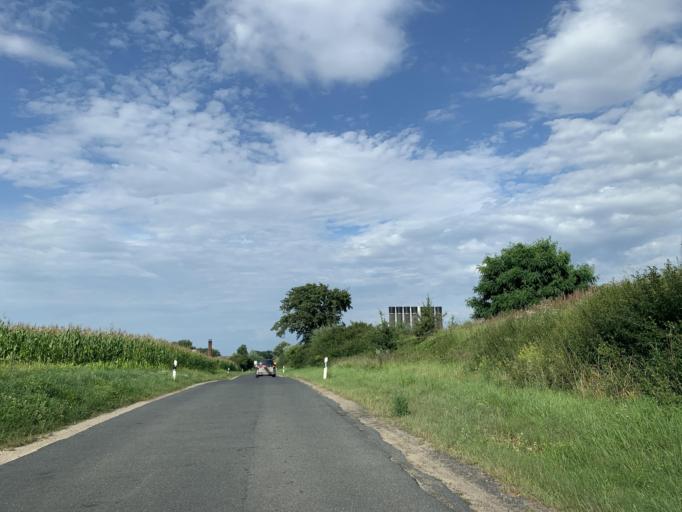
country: DE
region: Mecklenburg-Vorpommern
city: Carpin
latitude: 53.3884
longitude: 13.2186
